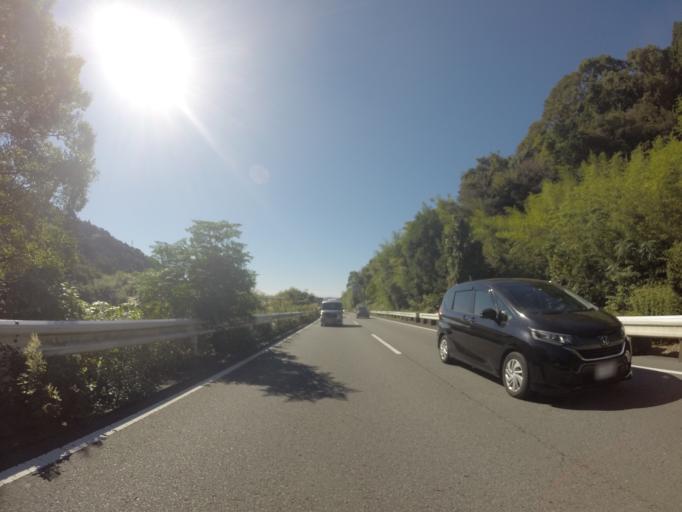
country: JP
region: Shizuoka
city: Fujieda
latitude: 34.9159
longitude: 138.2904
